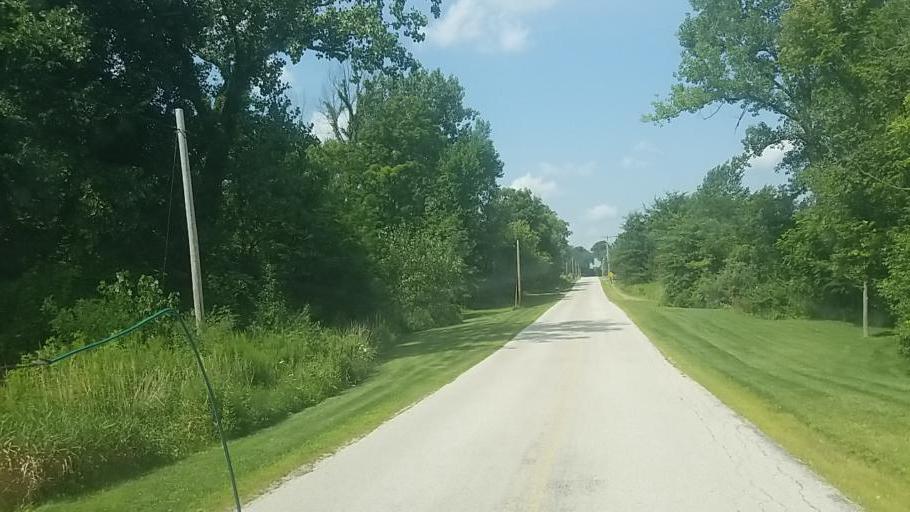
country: US
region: Ohio
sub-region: Richland County
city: Ontario
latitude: 40.7984
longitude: -82.6565
